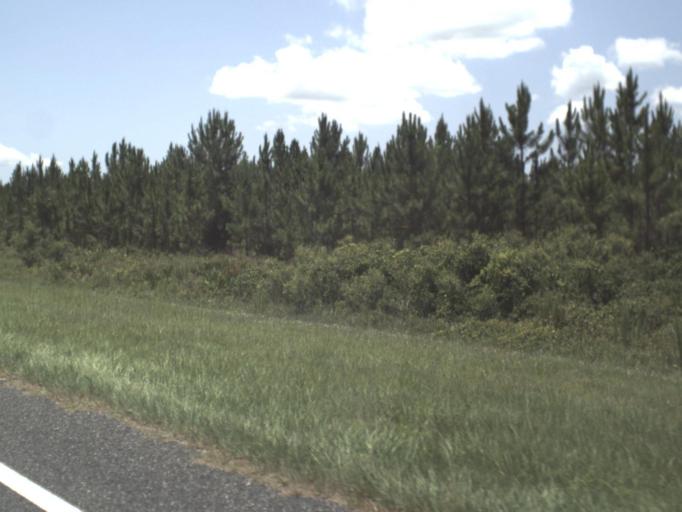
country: US
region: Florida
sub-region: Taylor County
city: Steinhatchee
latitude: 29.7654
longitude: -83.3226
